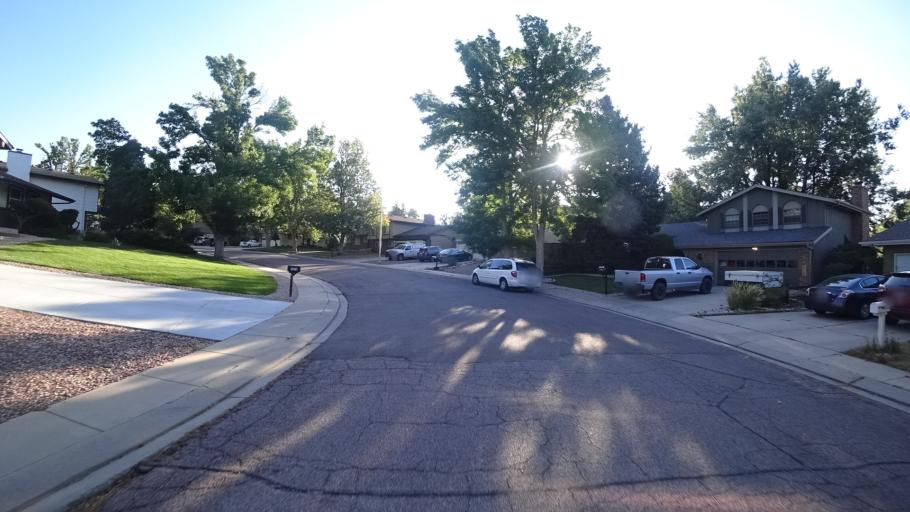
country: US
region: Colorado
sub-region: El Paso County
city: Cimarron Hills
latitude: 38.8830
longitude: -104.7478
